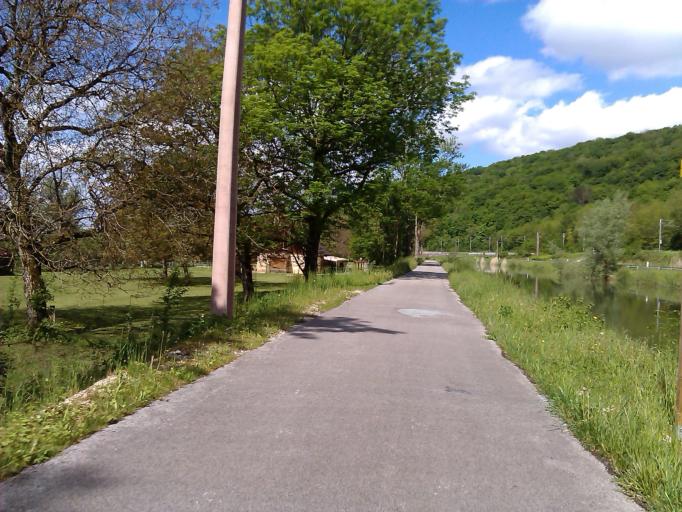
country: FR
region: Franche-Comte
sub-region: Departement du Doubs
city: Nancray
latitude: 47.2898
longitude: 6.1852
